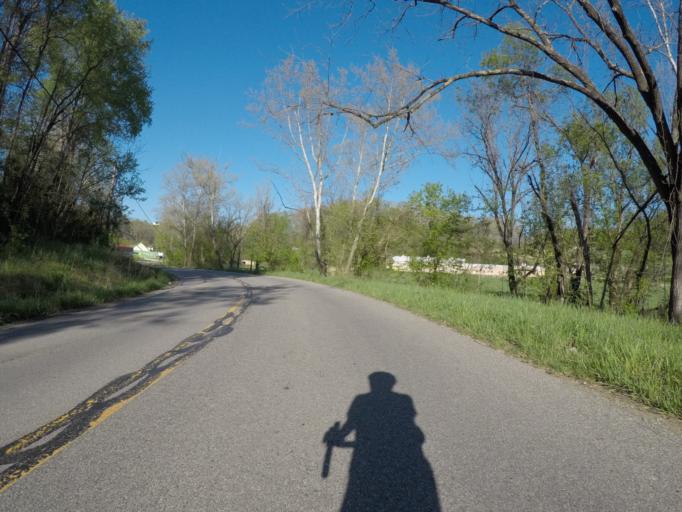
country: US
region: Kentucky
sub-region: Boyd County
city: Meads
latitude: 38.3567
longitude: -82.6950
